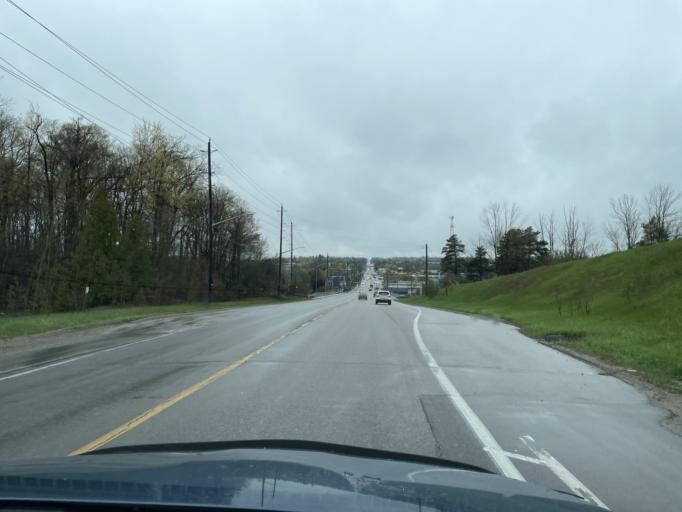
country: CA
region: Ontario
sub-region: Wellington County
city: Guelph
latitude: 43.5484
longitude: -80.2189
